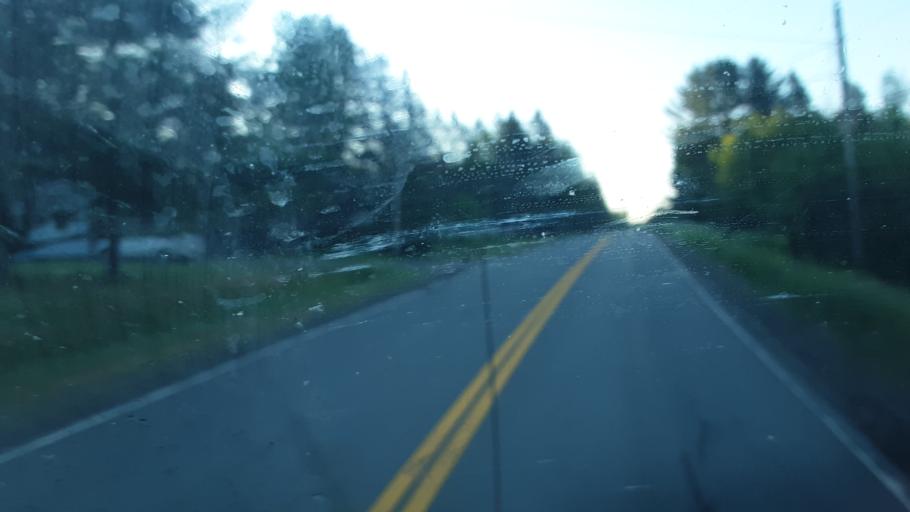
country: US
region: Maine
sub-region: Aroostook County
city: Presque Isle
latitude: 46.7557
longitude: -68.0621
